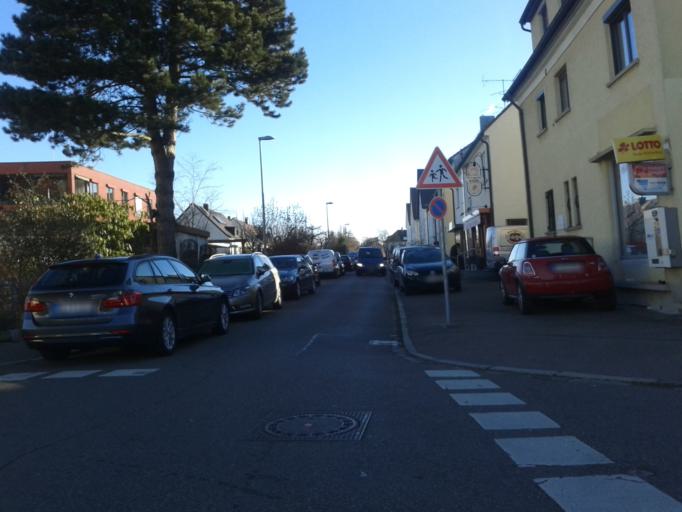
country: DE
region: Baden-Wuerttemberg
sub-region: Tuebingen Region
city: Ulm
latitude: 48.3903
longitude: 9.9638
